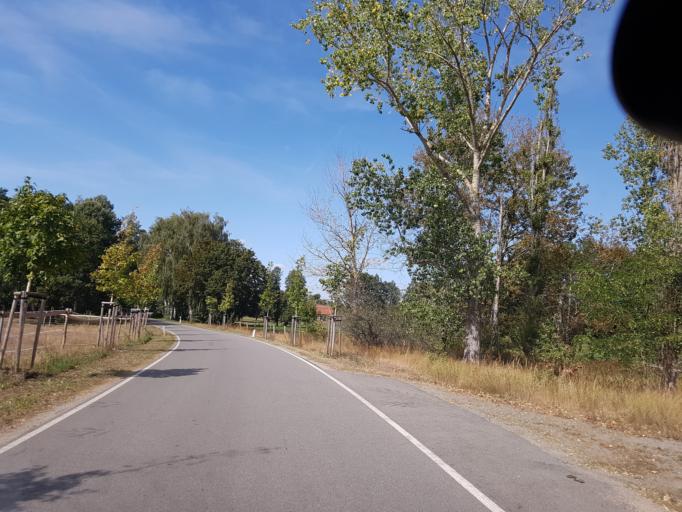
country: DE
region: Brandenburg
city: Drahnsdorf
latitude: 51.8577
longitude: 13.6305
